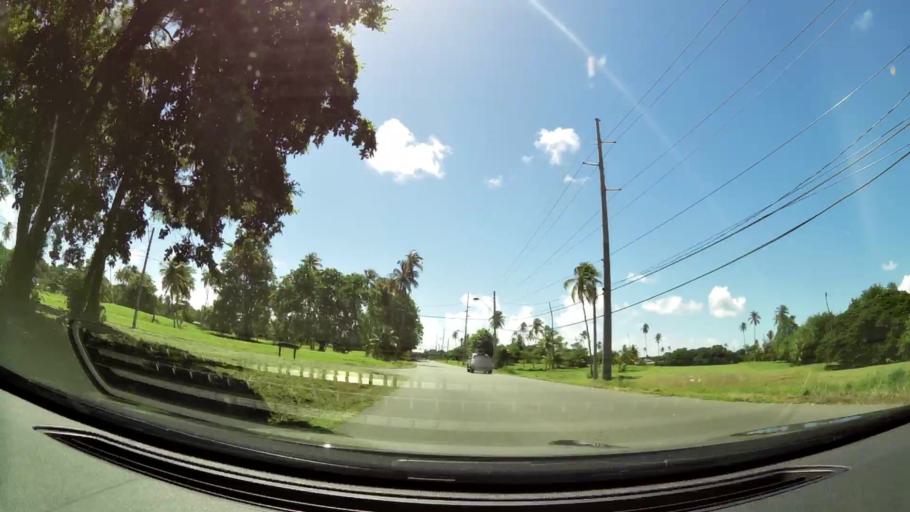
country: TT
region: Tobago
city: Scarborough
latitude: 11.1853
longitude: -60.7988
